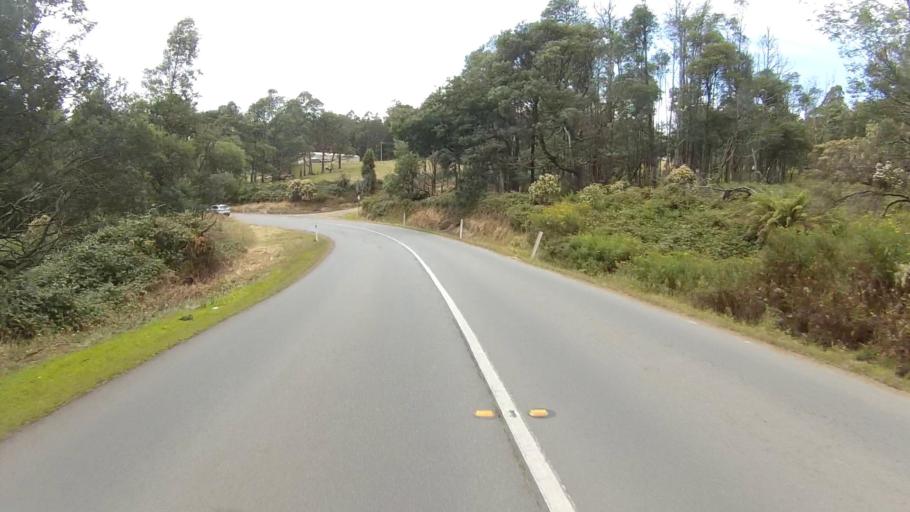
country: AU
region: Tasmania
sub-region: Kingborough
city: Kettering
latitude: -43.1104
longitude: 147.2011
